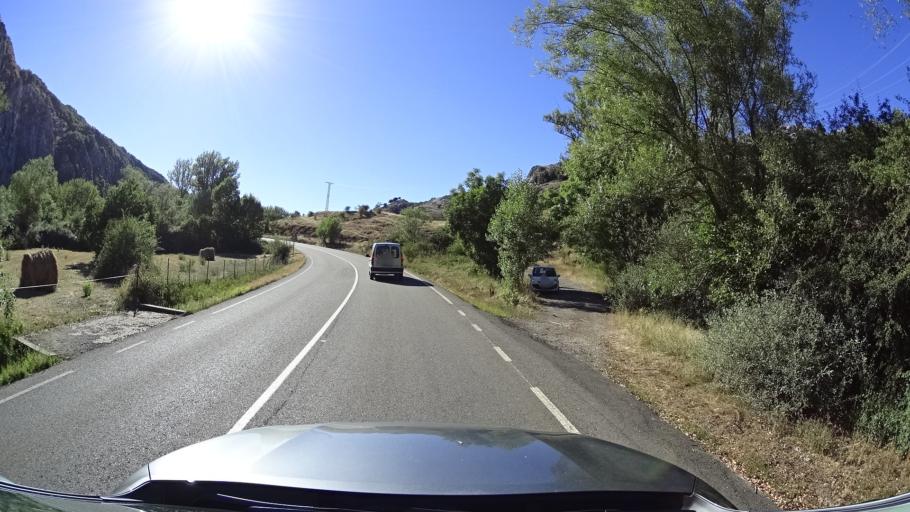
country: ES
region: Castille and Leon
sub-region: Provincia de Leon
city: La Pola de Gordon
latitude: 42.8693
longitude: -5.6828
